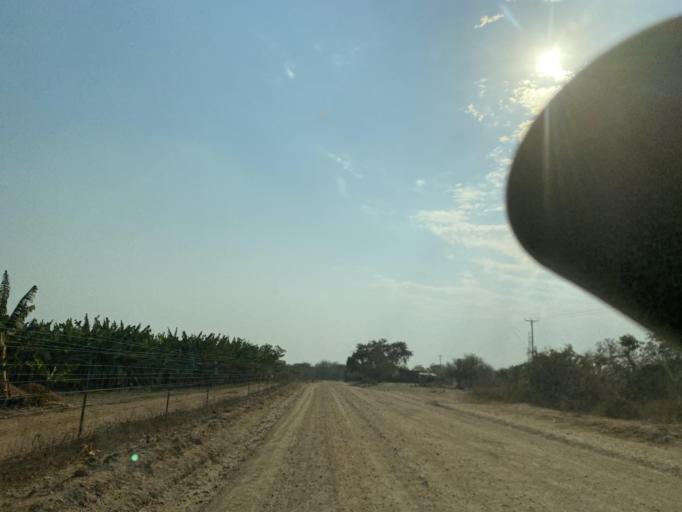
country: ZW
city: Chirundu
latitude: -15.9342
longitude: 28.9430
